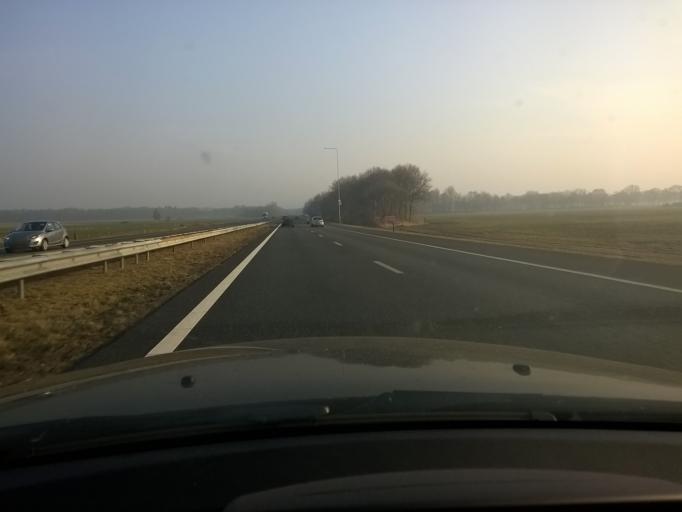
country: NL
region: Drenthe
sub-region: Gemeente Tynaarlo
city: Vries
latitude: 53.0504
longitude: 6.5927
